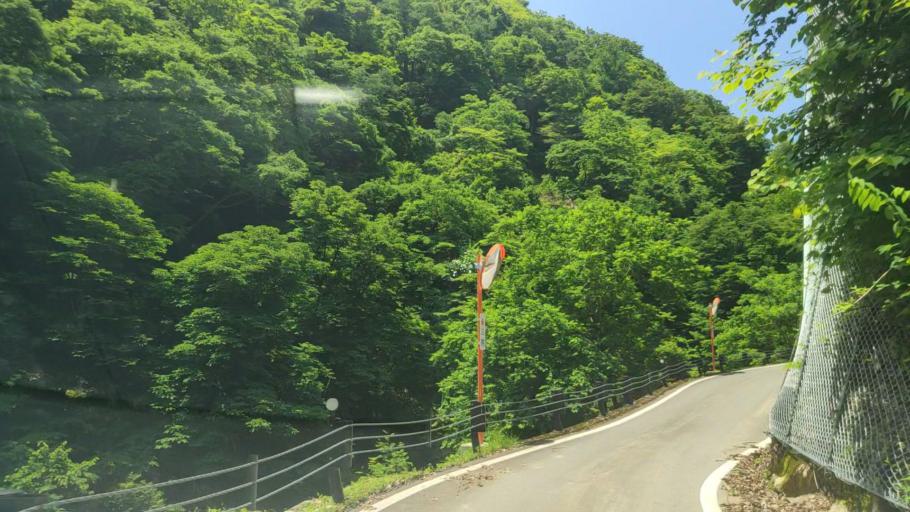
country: JP
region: Tottori
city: Tottori
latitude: 35.4043
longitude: 134.5059
